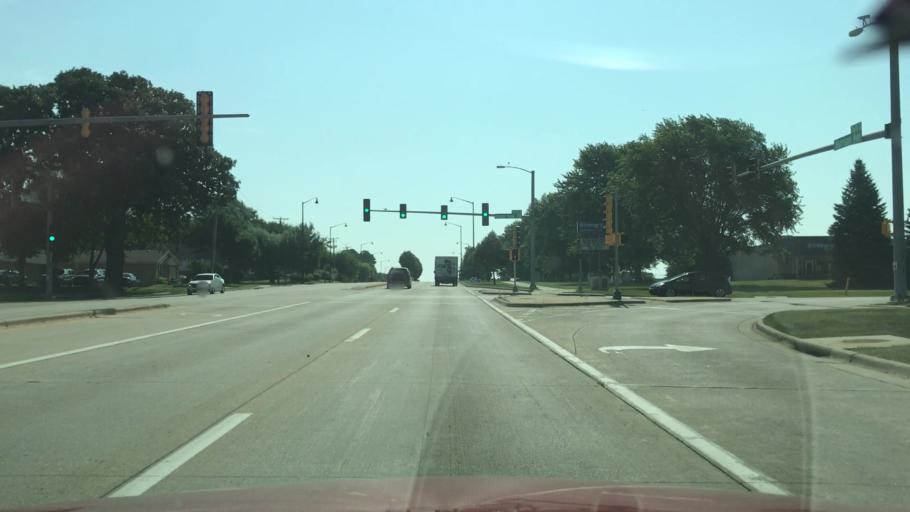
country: US
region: Illinois
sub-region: Winnebago County
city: Cherry Valley
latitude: 42.2382
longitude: -89.0197
